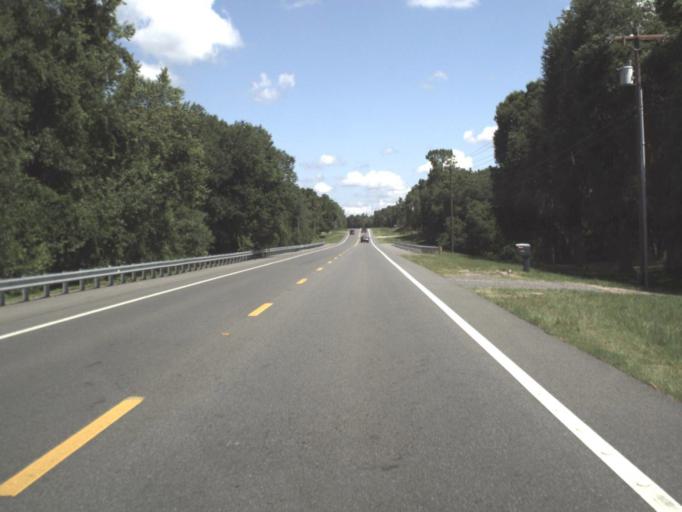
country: US
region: Florida
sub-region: Clay County
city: Keystone Heights
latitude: 29.7513
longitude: -81.9949
